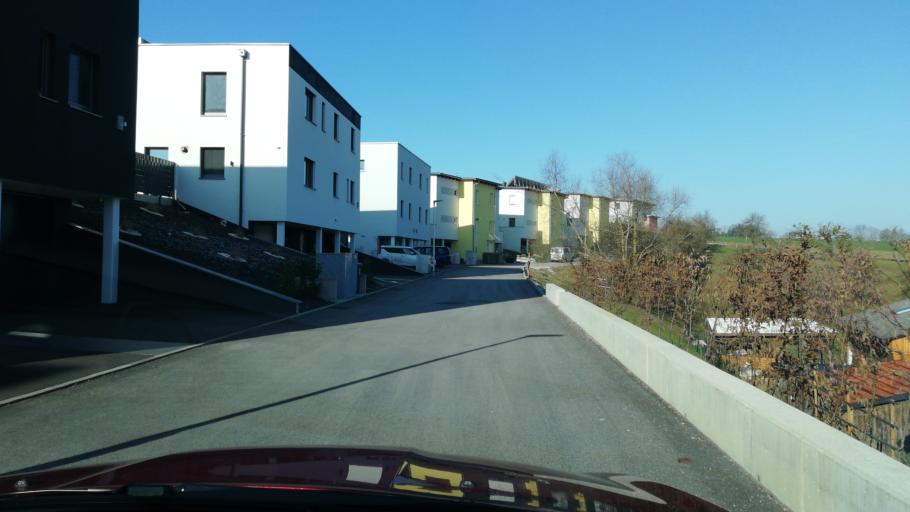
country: AT
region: Upper Austria
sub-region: Politischer Bezirk Kirchdorf an der Krems
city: Kremsmunster
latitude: 48.0569
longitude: 14.1249
